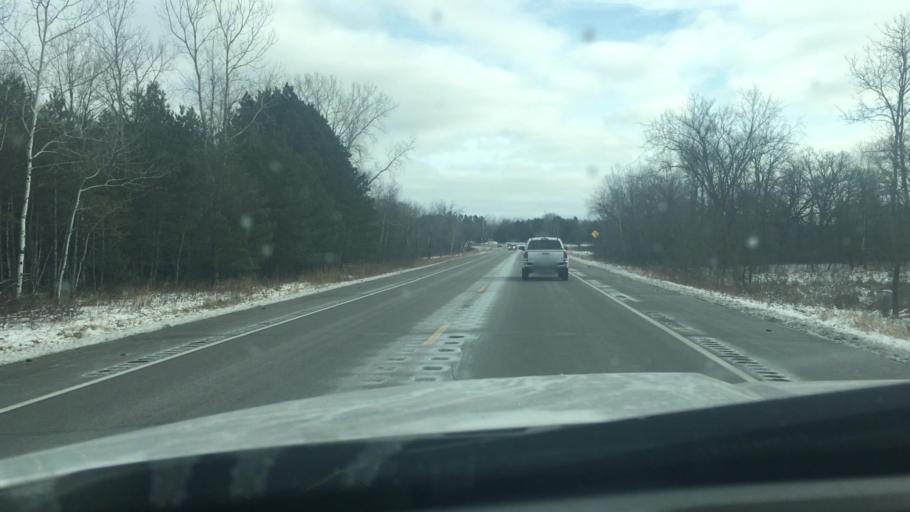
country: US
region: Minnesota
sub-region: Isanti County
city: Cambridge
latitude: 45.5760
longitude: -93.3155
